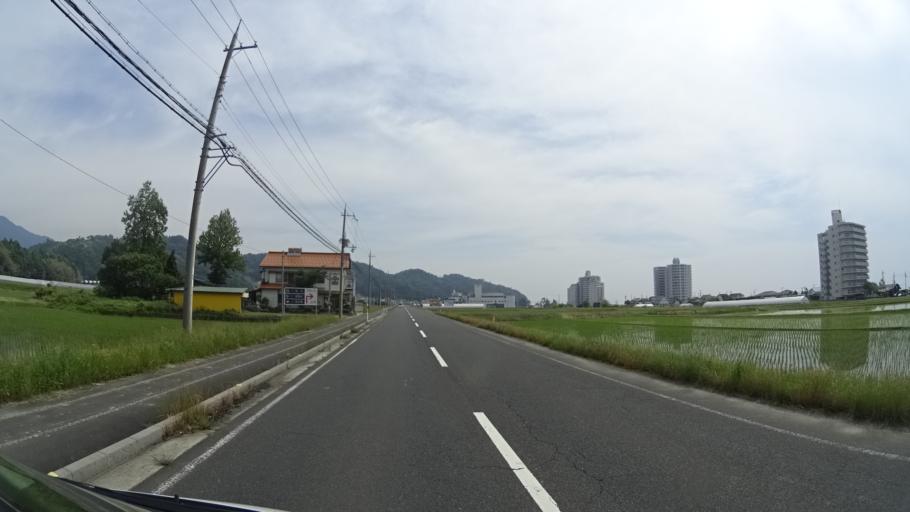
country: JP
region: Kyoto
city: Miyazu
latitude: 35.6103
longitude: 135.2275
